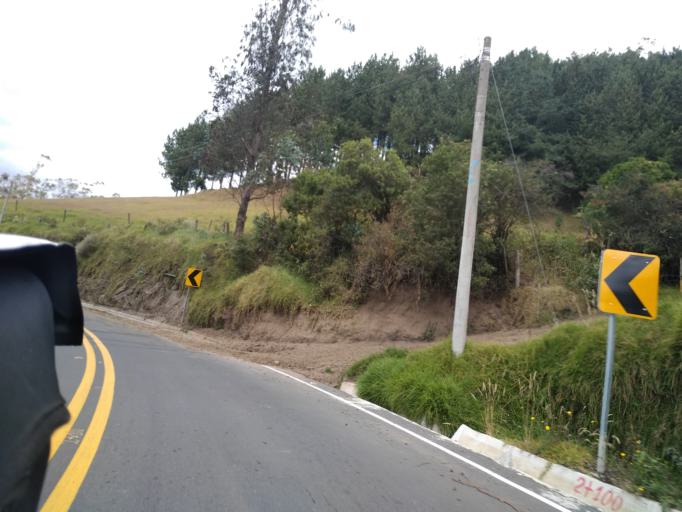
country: EC
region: Cotopaxi
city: Saquisili
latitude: -0.7163
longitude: -78.8872
